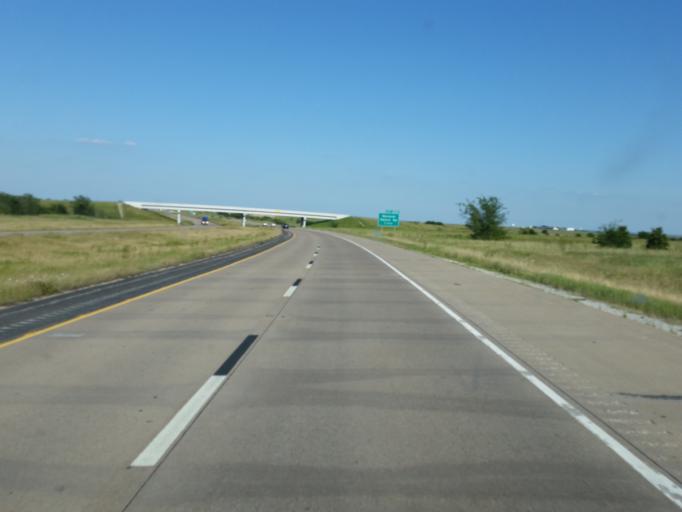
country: US
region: Texas
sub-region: Parker County
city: Aledo
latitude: 32.6975
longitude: -97.5410
